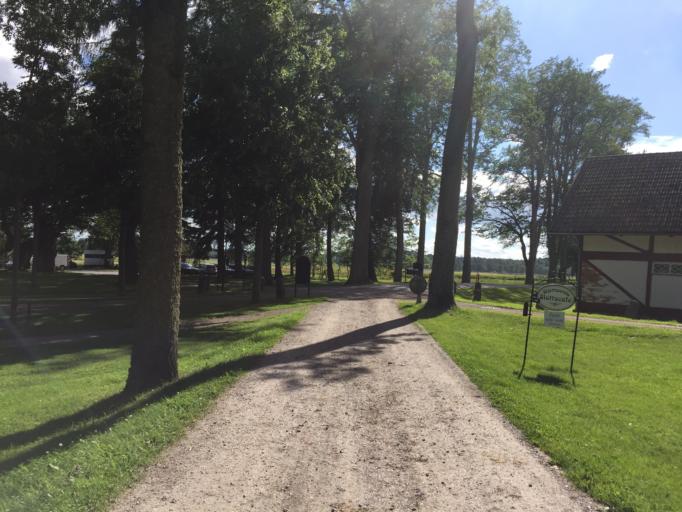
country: SE
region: OErebro
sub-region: Askersunds Kommun
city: Askersund
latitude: 58.8508
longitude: 14.9341
